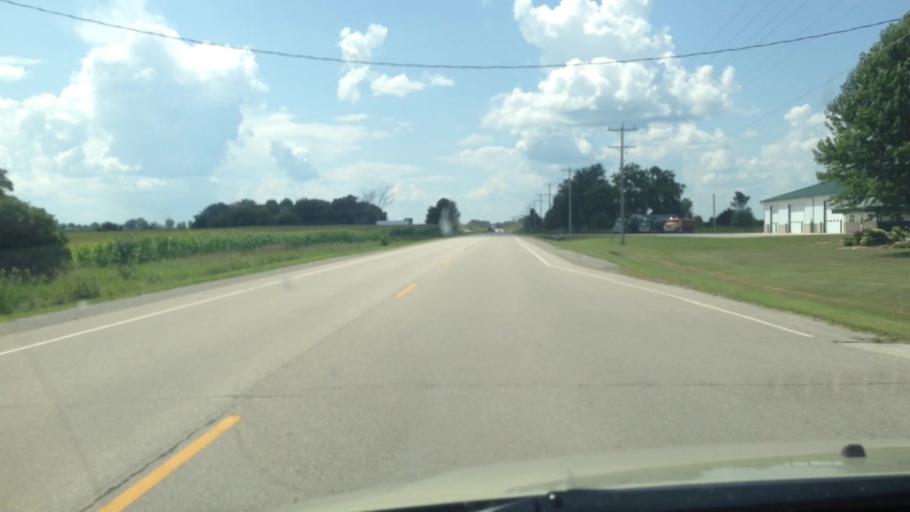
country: US
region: Wisconsin
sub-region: Brown County
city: Pulaski
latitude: 44.6735
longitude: -88.2928
